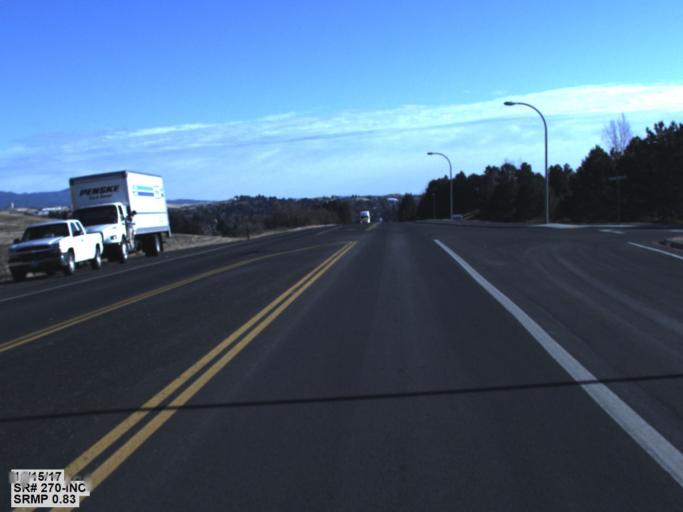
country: US
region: Washington
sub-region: Whitman County
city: Pullman
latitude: 46.7337
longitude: -117.2093
